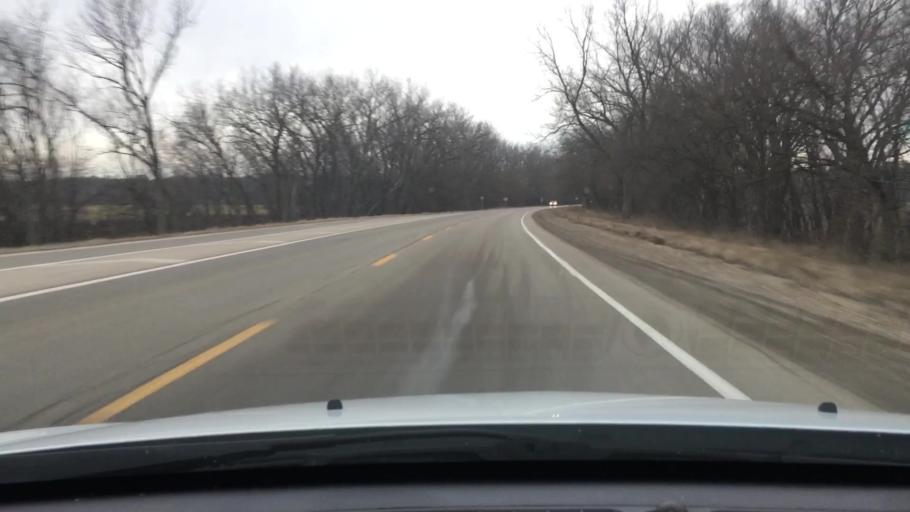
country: US
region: Illinois
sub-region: LaSalle County
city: Peru
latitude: 41.3146
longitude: -89.1188
